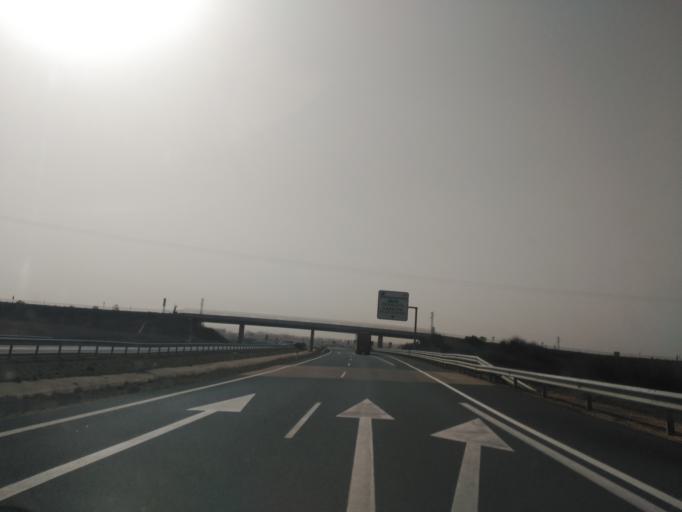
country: ES
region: Castille and Leon
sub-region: Provincia de Palencia
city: Fromista
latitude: 42.2669
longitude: -4.4158
